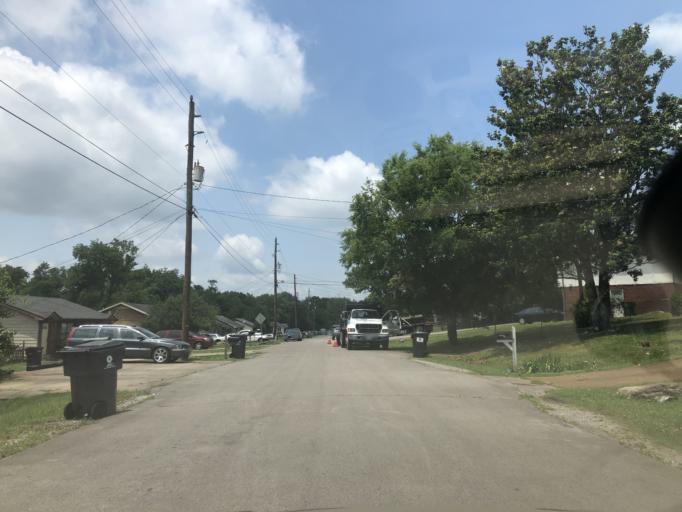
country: US
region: Tennessee
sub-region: Davidson County
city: Lakewood
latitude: 36.2101
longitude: -86.6290
